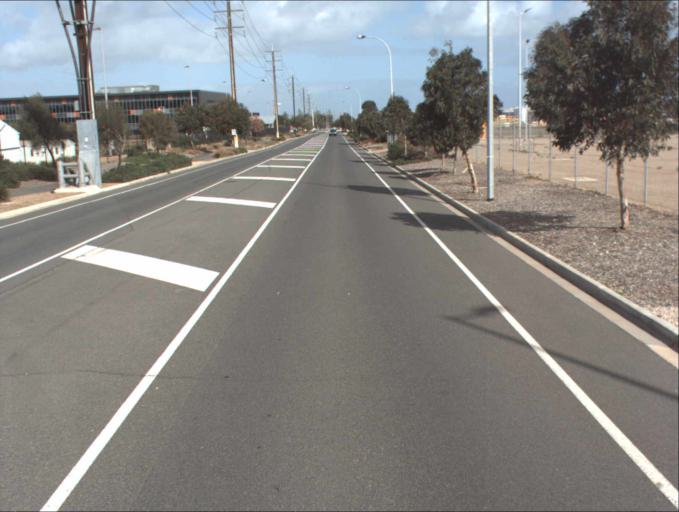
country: AU
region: South Australia
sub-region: Port Adelaide Enfield
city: Birkenhead
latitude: -34.7854
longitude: 138.5071
